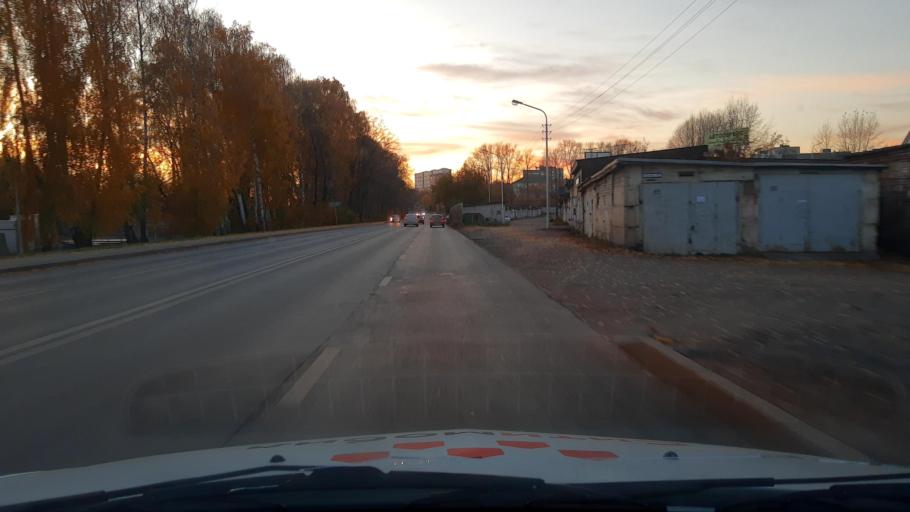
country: RU
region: Bashkortostan
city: Ufa
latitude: 54.8107
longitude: 56.0798
